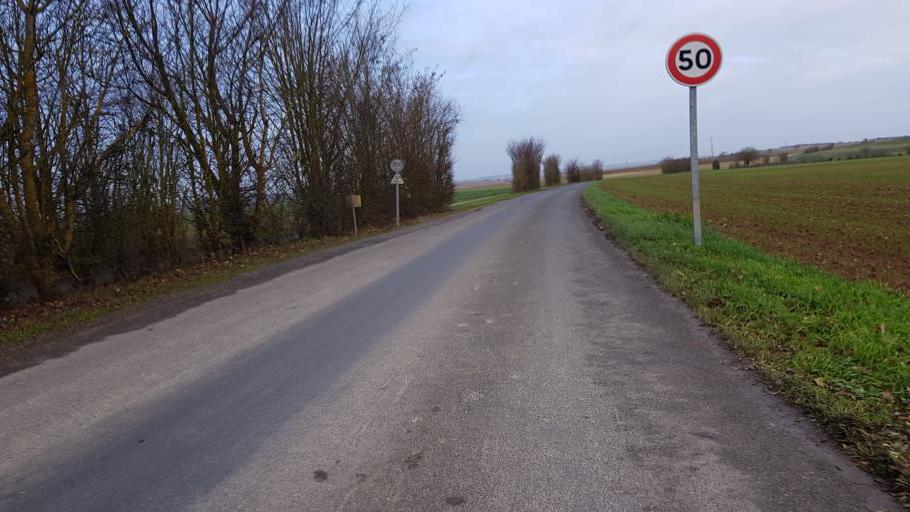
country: FR
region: Poitou-Charentes
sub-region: Departement de la Vienne
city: Avanton
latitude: 46.6671
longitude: 0.3129
